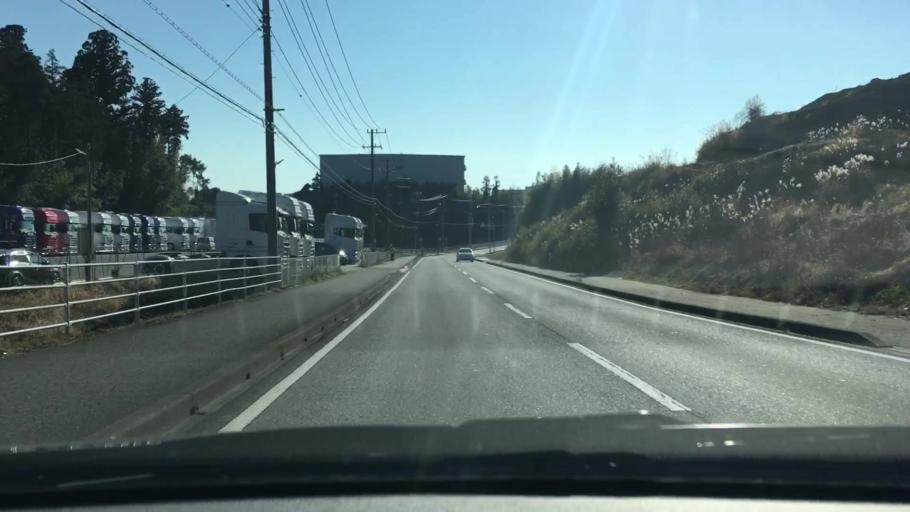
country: JP
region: Chiba
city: Shisui
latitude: 35.7196
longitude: 140.3246
